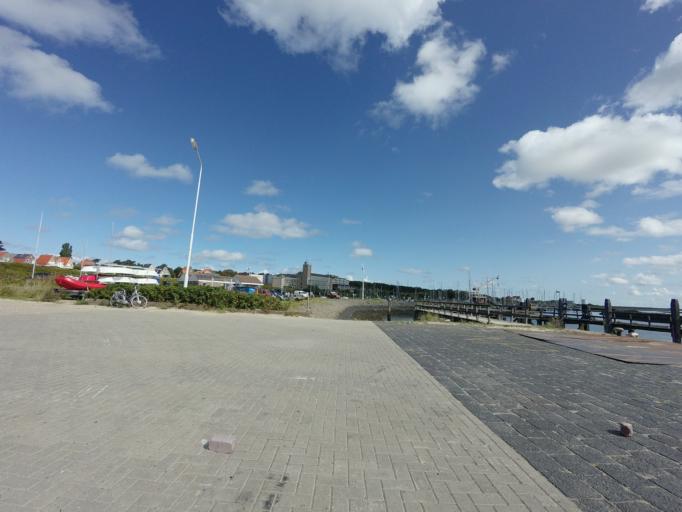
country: NL
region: Friesland
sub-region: Gemeente Terschelling
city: West-Terschelling
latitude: 53.3637
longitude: 5.2204
